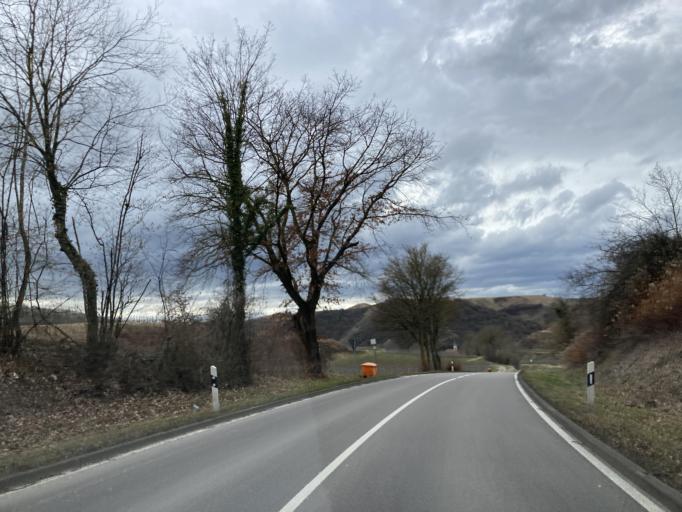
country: DE
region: Baden-Wuerttemberg
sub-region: Freiburg Region
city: Botzingen
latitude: 48.0869
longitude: 7.6902
